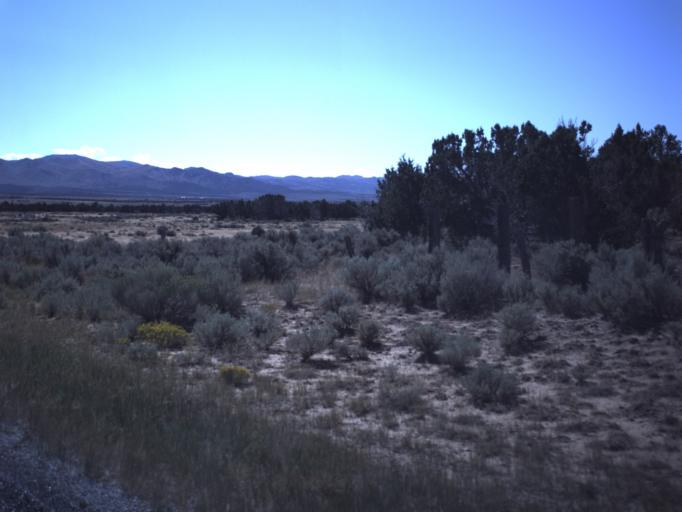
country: US
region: Utah
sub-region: Utah County
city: Genola
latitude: 39.9338
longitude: -112.1732
